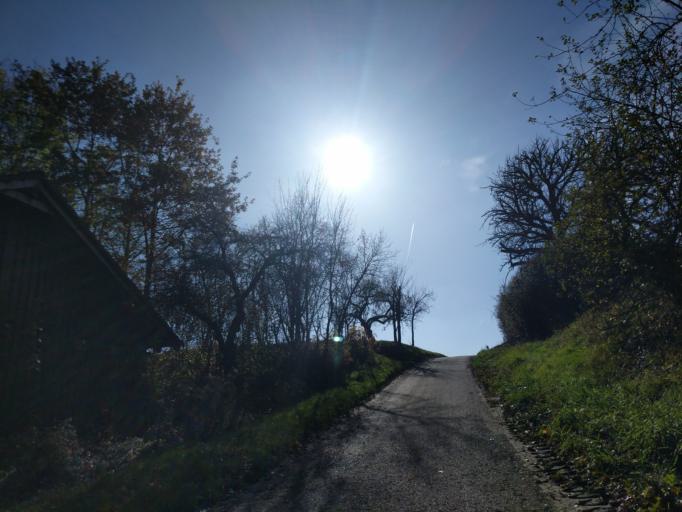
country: DE
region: Baden-Wuerttemberg
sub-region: Tuebingen Region
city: Rottenburg
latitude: 48.5012
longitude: 8.9604
